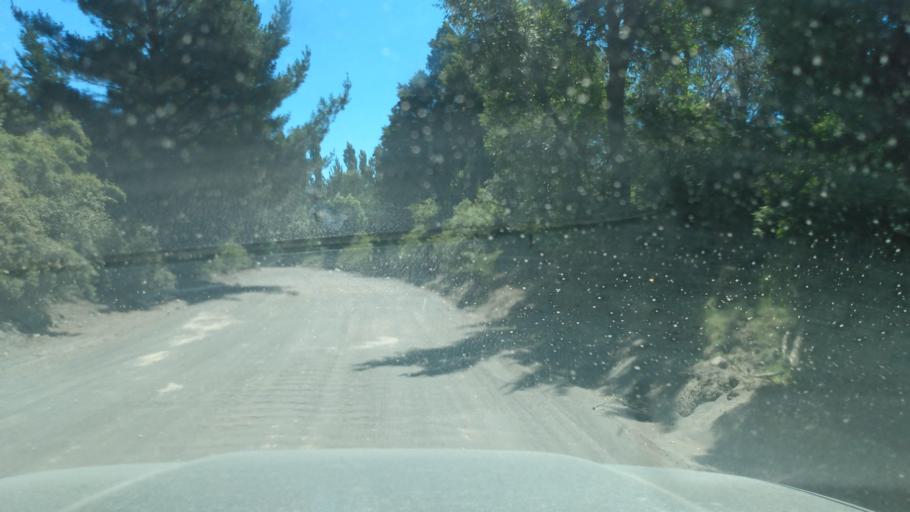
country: AR
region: Neuquen
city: Villa La Angostura
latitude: -40.6283
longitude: -71.4804
